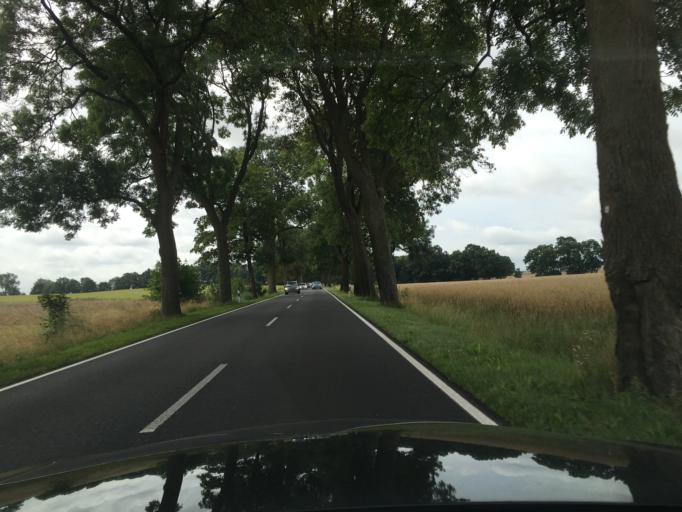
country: DE
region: Brandenburg
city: Gransee
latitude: 52.9561
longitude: 13.1506
